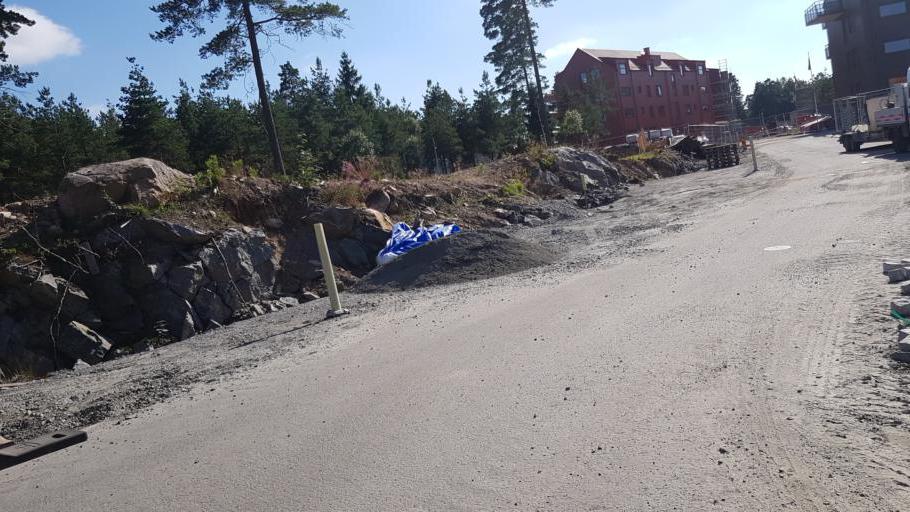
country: SE
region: Vaestra Goetaland
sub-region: Partille Kommun
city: Furulund
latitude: 57.6993
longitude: 12.1457
